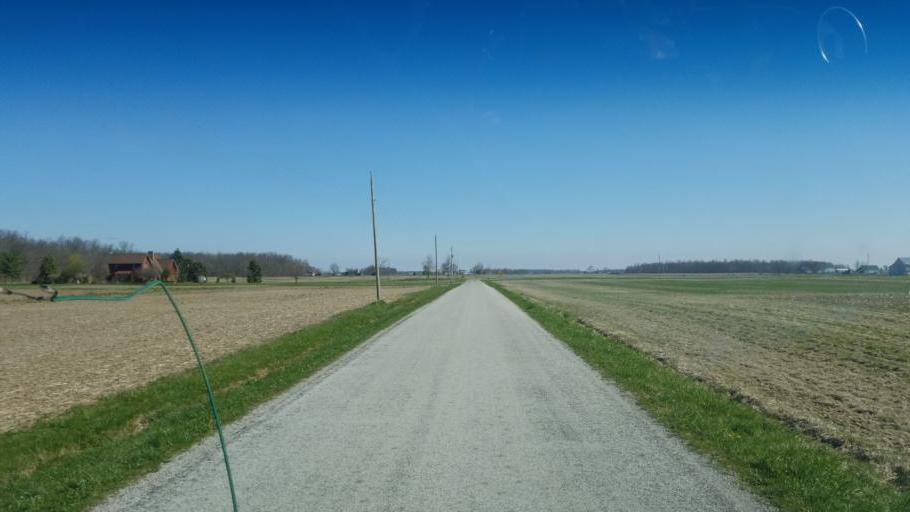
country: US
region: Ohio
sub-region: Hardin County
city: Kenton
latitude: 40.6780
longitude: -83.5617
